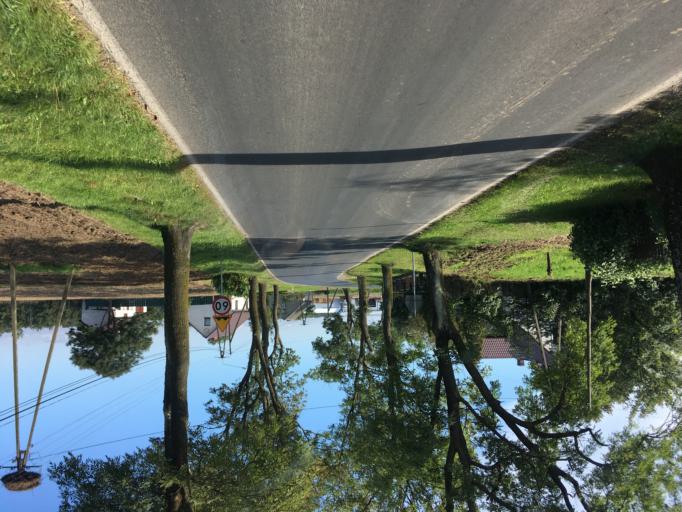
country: PL
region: Kujawsko-Pomorskie
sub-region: Powiat swiecki
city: Lniano
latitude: 53.5199
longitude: 18.1928
